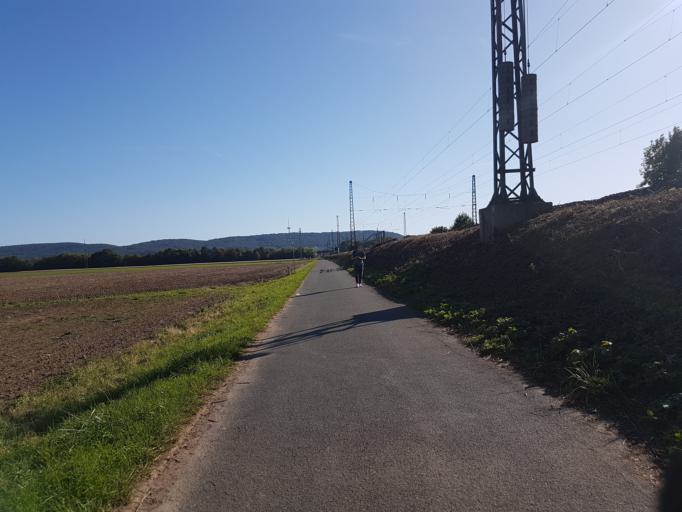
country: DE
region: North Rhine-Westphalia
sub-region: Regierungsbezirk Detmold
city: Minden
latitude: 52.2791
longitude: 8.9331
